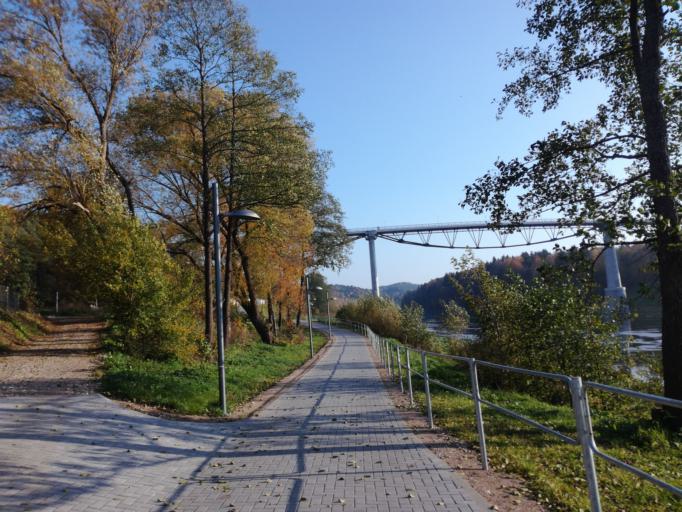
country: LT
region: Alytaus apskritis
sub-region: Alytus
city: Alytus
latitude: 54.3950
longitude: 24.0799
